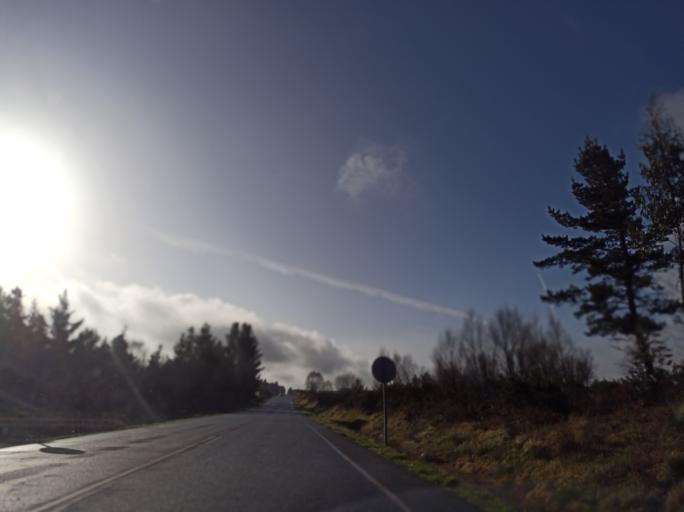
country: ES
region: Galicia
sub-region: Provincia da Coruna
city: Curtis
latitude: 43.1185
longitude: -8.0283
